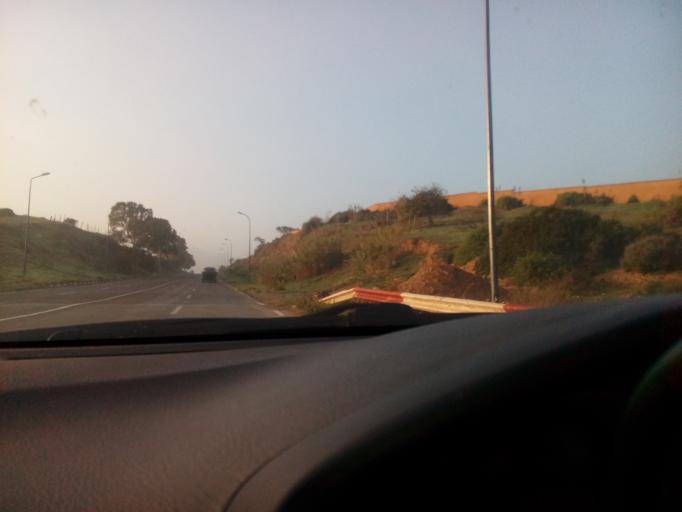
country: DZ
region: Oran
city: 'Ain el Turk
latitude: 35.7187
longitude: -0.8523
